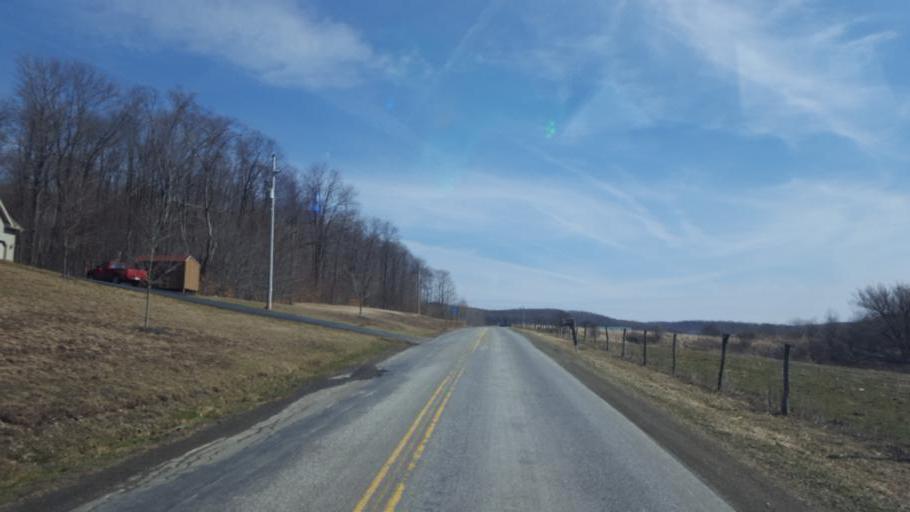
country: US
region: Pennsylvania
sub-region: Potter County
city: Galeton
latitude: 41.8948
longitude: -77.7550
